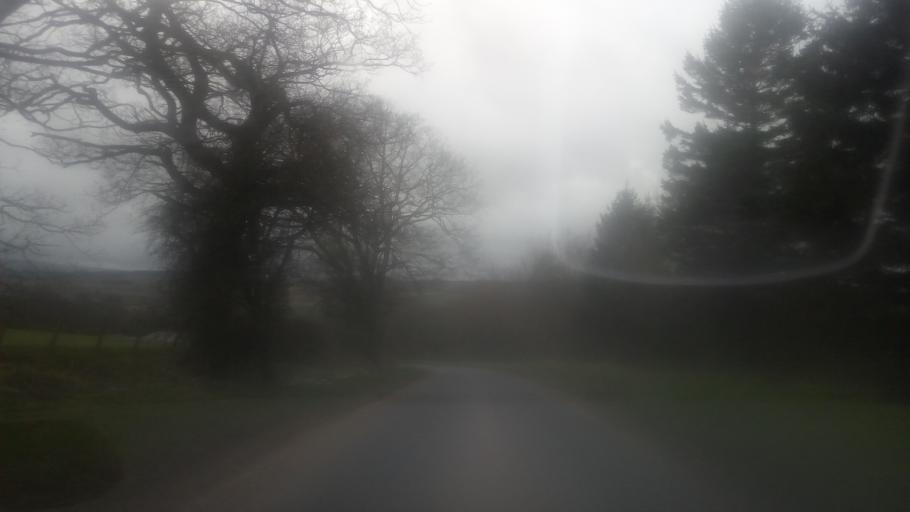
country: GB
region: Scotland
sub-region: The Scottish Borders
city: Jedburgh
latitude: 55.4956
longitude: -2.4785
